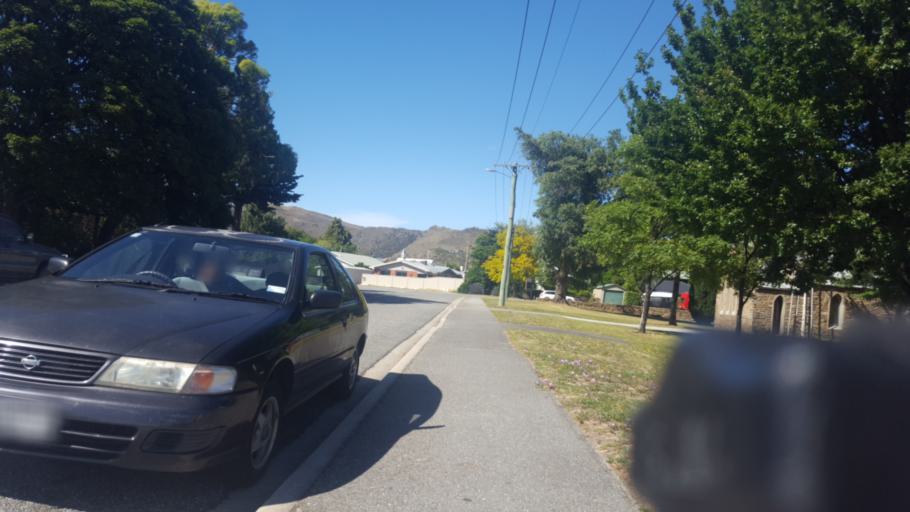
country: NZ
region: Otago
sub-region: Queenstown-Lakes District
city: Wanaka
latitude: -45.0470
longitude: 169.2102
